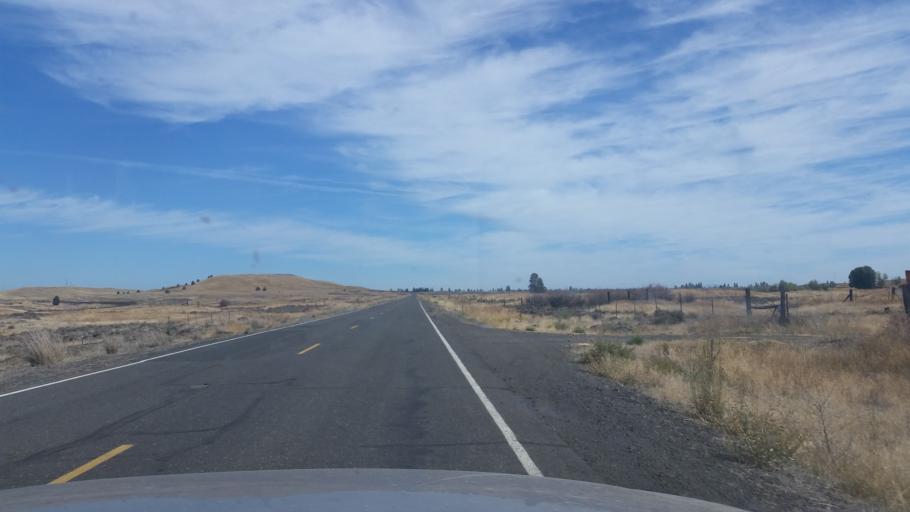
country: US
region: Washington
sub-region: Spokane County
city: Medical Lake
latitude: 47.3446
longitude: -117.8672
